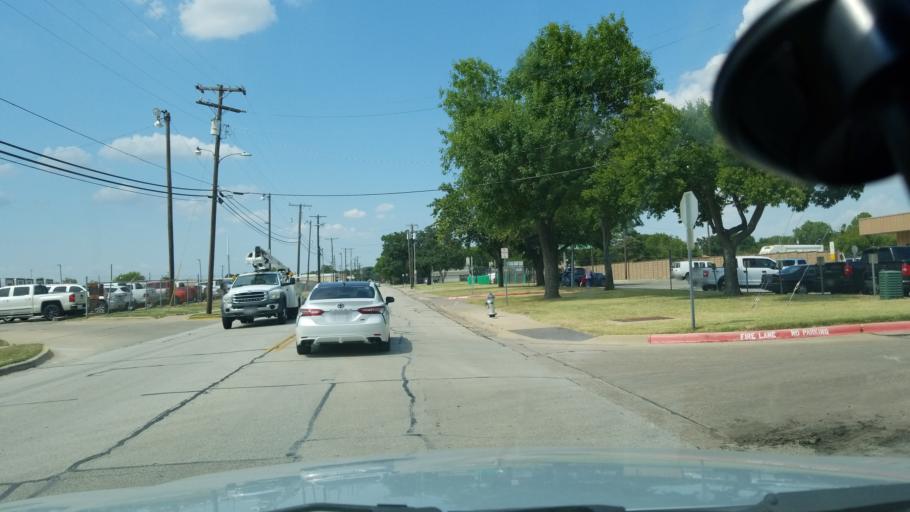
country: US
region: Texas
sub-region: Dallas County
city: Irving
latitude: 32.8169
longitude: -96.9895
